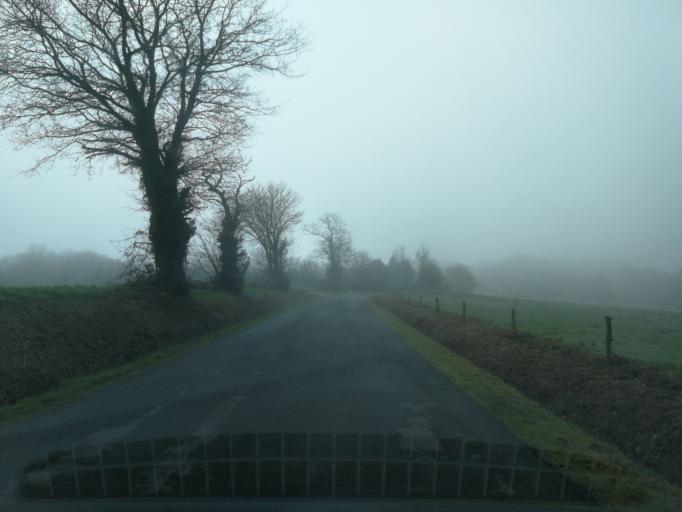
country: FR
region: Brittany
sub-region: Departement du Morbihan
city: La Vraie-Croix
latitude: 47.7221
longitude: -2.5114
